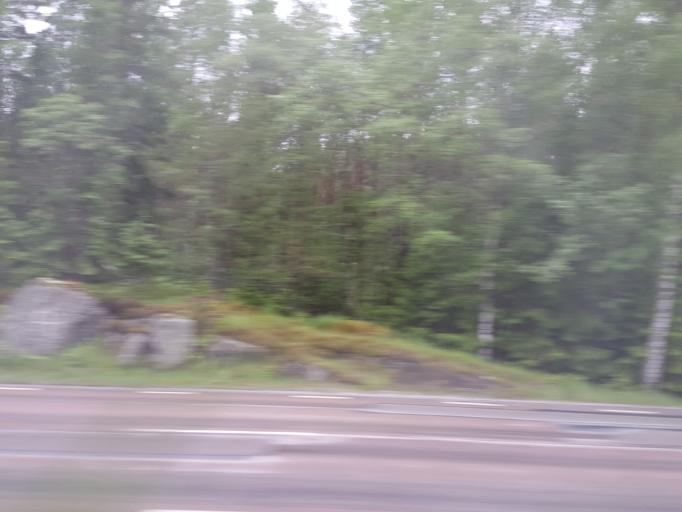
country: SE
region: Vaestmanland
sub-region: Sala Kommun
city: Sala
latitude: 59.9489
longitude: 16.5369
